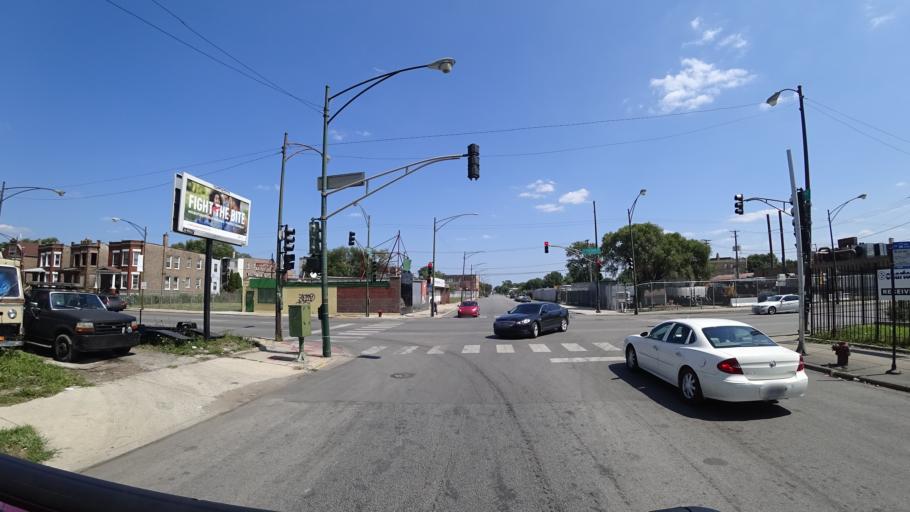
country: US
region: Illinois
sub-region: Cook County
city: Cicero
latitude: 41.8588
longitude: -87.7350
